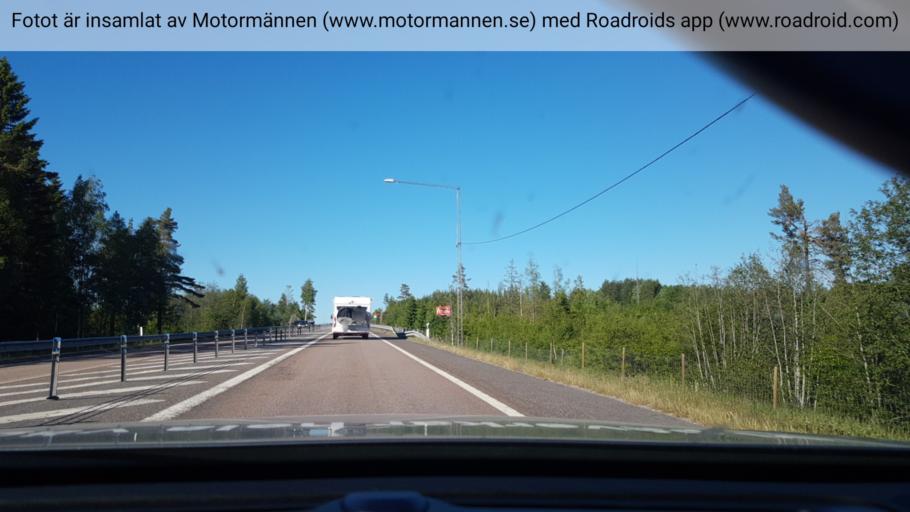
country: SE
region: Vaesternorrland
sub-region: Haernoesands Kommun
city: Haernoesand
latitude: 62.5995
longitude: 17.8101
